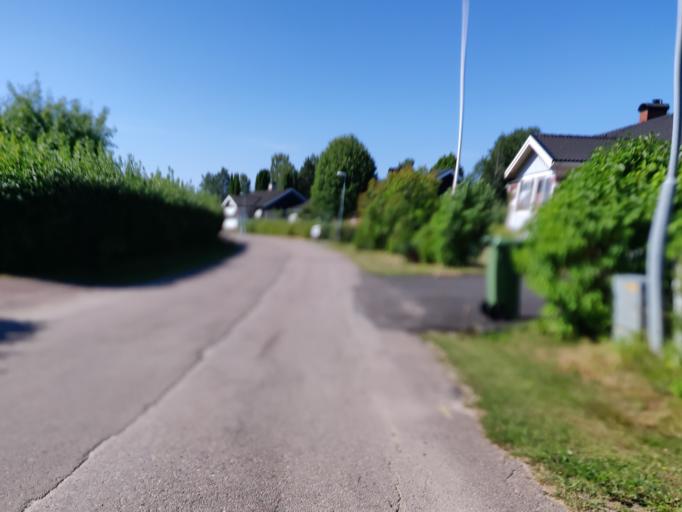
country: SE
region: Vaermland
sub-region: Hagfors Kommun
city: Hagfors
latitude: 60.0002
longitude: 13.5890
